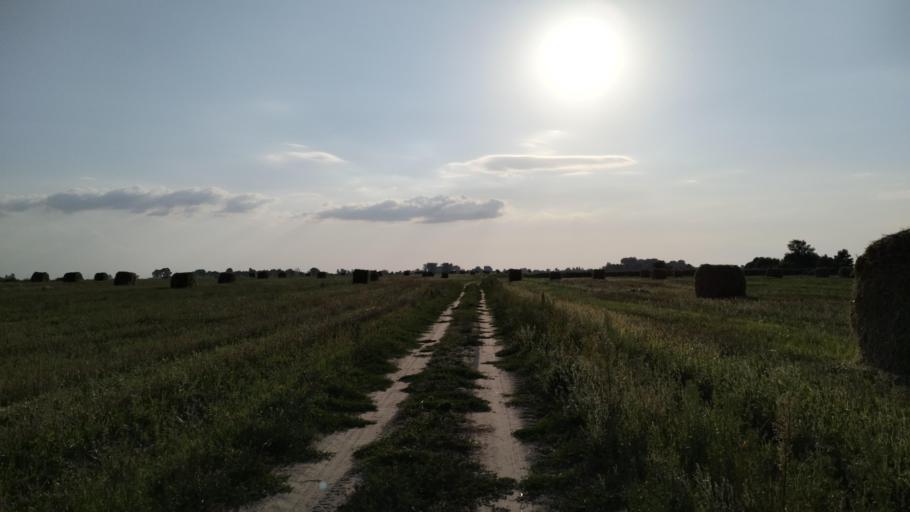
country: BY
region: Brest
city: Davyd-Haradok
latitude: 52.0247
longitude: 27.1977
